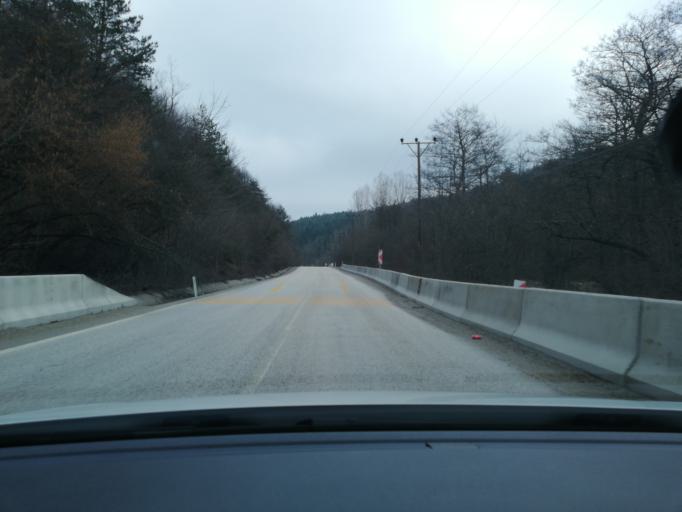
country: TR
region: Duzce
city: Kaynasli
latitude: 40.6829
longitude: 31.4470
